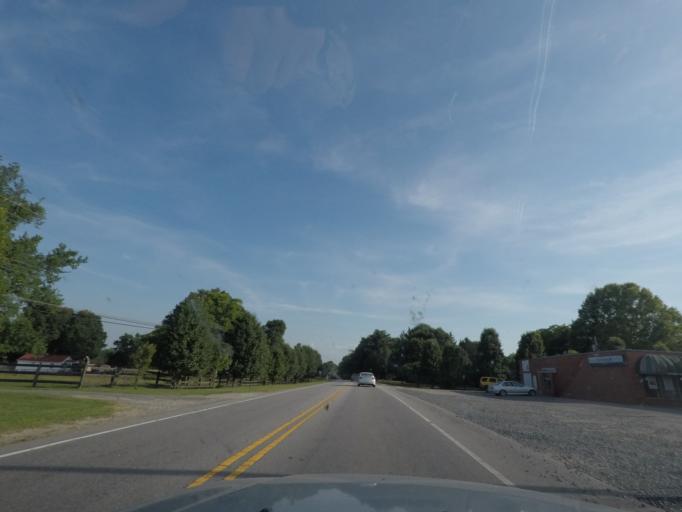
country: US
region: North Carolina
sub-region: Granville County
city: Oxford
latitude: 36.2911
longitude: -78.6041
